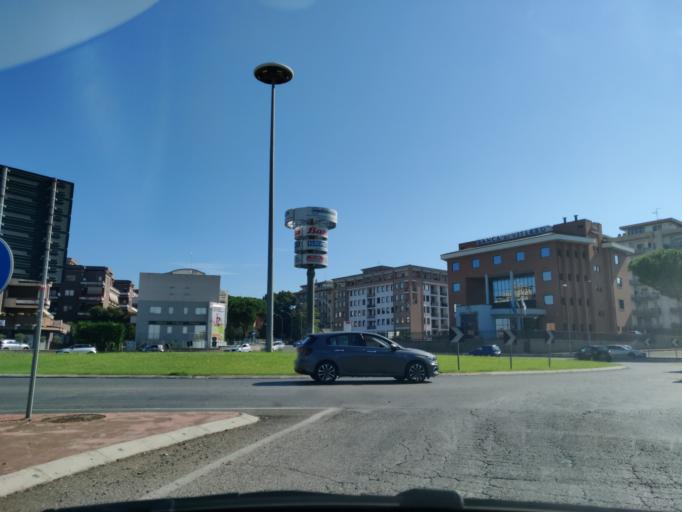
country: IT
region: Latium
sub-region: Provincia di Viterbo
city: Viterbo
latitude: 42.4266
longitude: 12.0985
